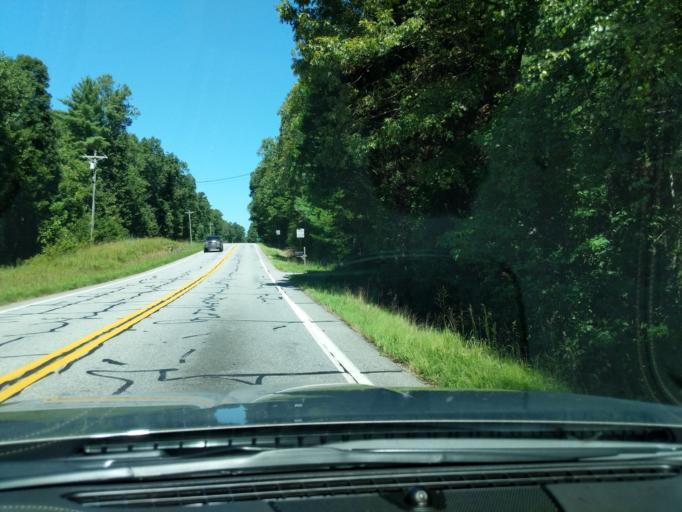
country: US
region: Georgia
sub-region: Habersham County
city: Clarkesville
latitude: 34.6677
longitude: -83.6481
